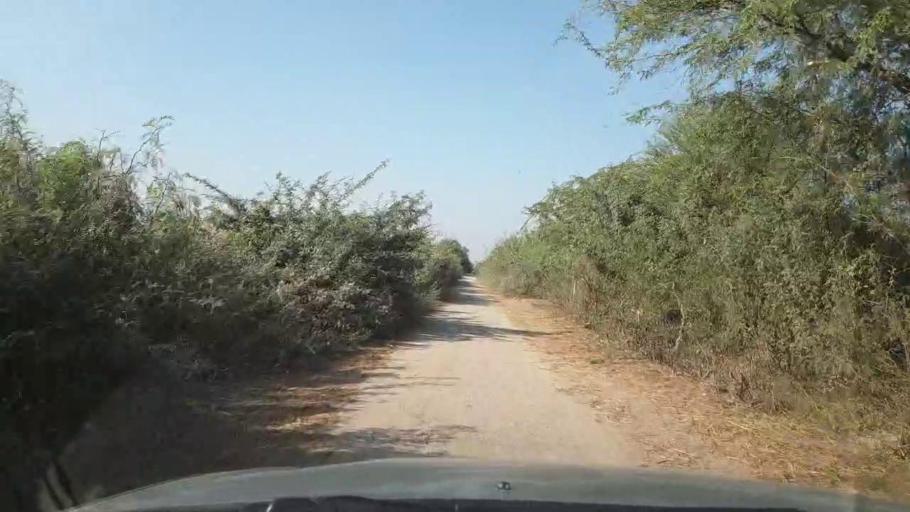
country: PK
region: Sindh
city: Tando Muhammad Khan
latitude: 25.1082
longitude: 68.5898
